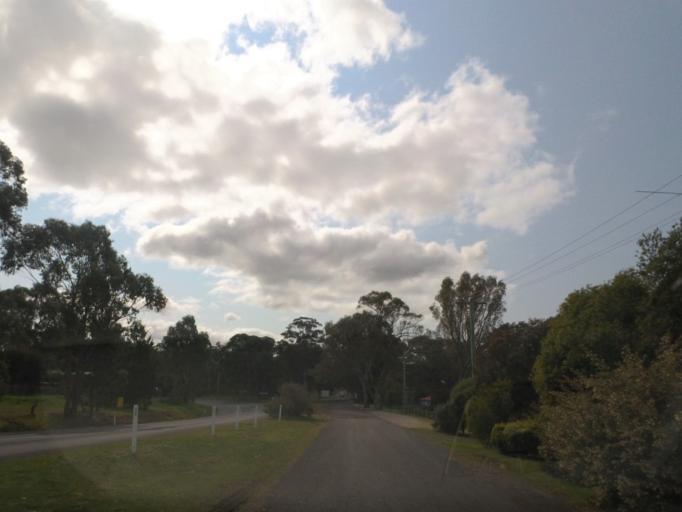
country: AU
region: Victoria
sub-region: Murrindindi
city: Kinglake West
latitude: -37.0927
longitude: 145.1043
